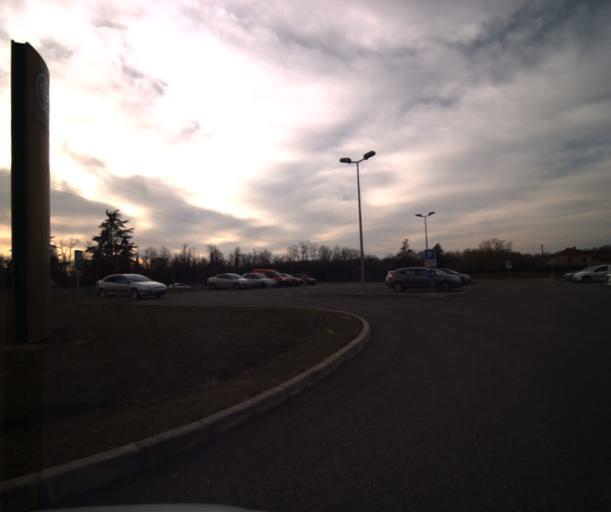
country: FR
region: Midi-Pyrenees
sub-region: Departement du Tarn-et-Garonne
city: Finhan
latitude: 43.9246
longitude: 1.2614
